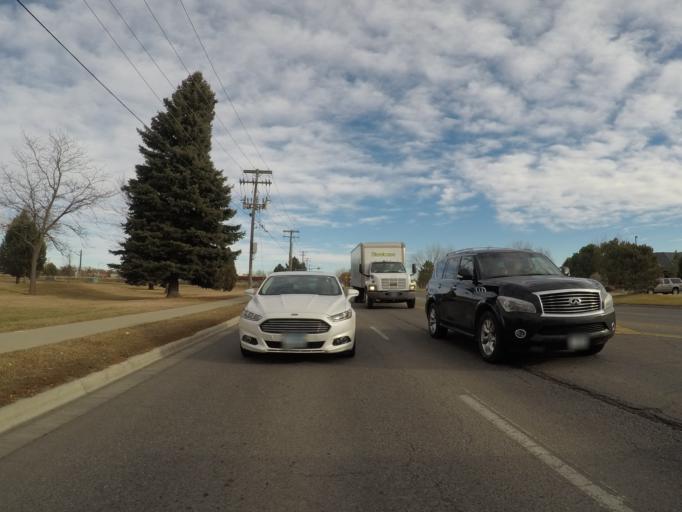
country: US
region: Montana
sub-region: Yellowstone County
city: Billings
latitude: 45.7698
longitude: -108.5879
